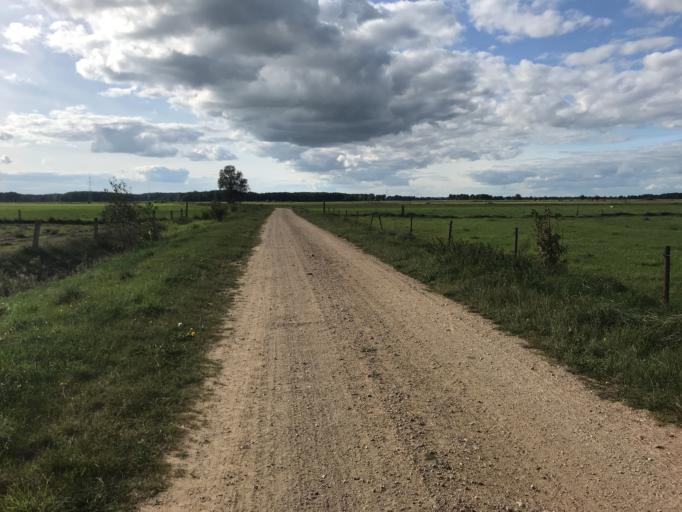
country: PL
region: Podlasie
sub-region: Powiat zambrowski
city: Rutki
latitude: 53.2018
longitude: 22.5847
